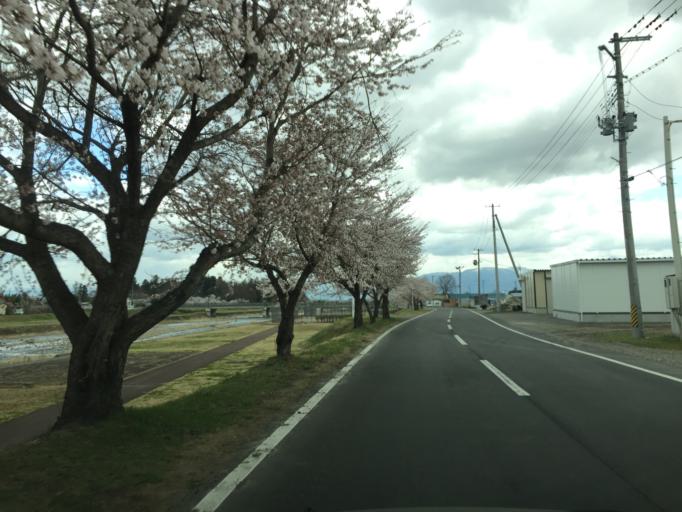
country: JP
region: Fukushima
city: Kitakata
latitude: 37.4505
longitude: 139.8389
